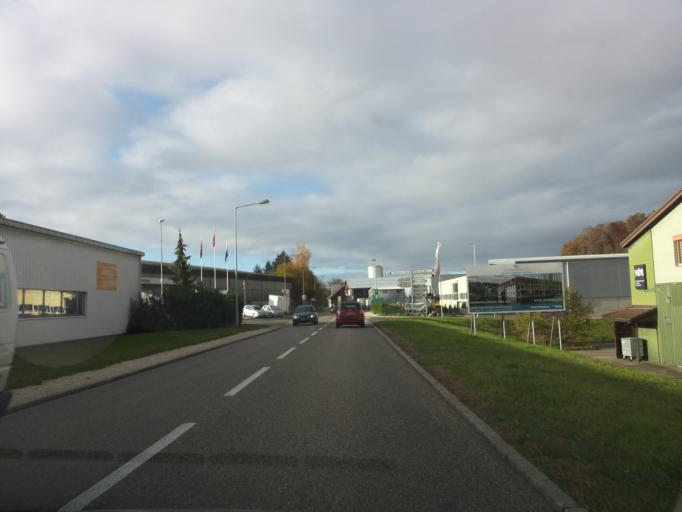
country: CH
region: Lucerne
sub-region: Willisau District
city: Pfaffnau
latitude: 47.2349
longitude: 7.9109
